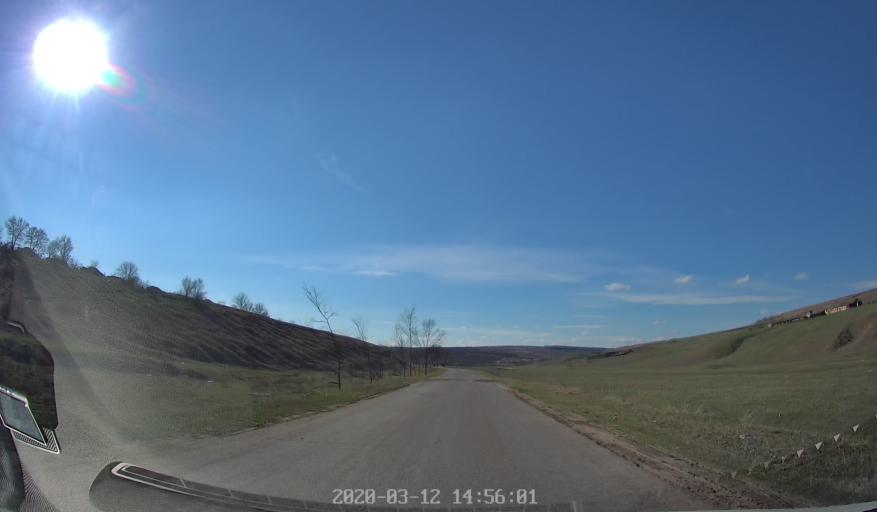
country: MD
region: Telenesti
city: Cocieri
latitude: 47.2246
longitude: 29.0544
